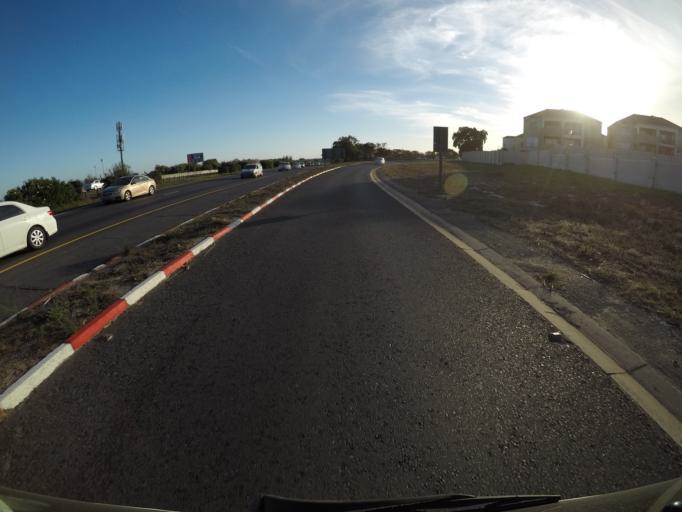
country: ZA
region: Western Cape
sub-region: City of Cape Town
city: Kraaifontein
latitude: -33.8637
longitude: 18.6863
